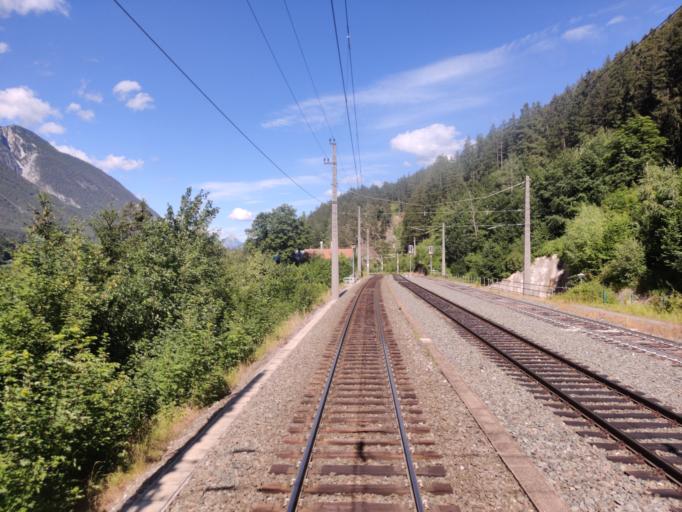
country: AT
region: Tyrol
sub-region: Politischer Bezirk Landeck
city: Pians
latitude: 47.1302
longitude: 10.5102
